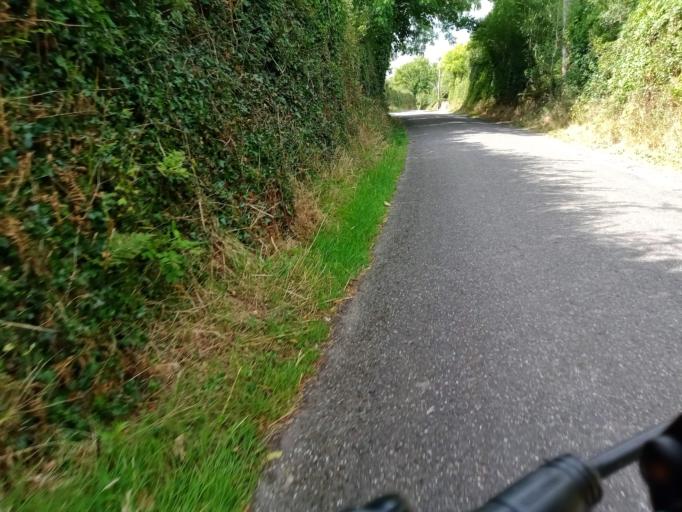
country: IE
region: Munster
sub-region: Waterford
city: Dungarvan
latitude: 52.1396
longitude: -7.4863
